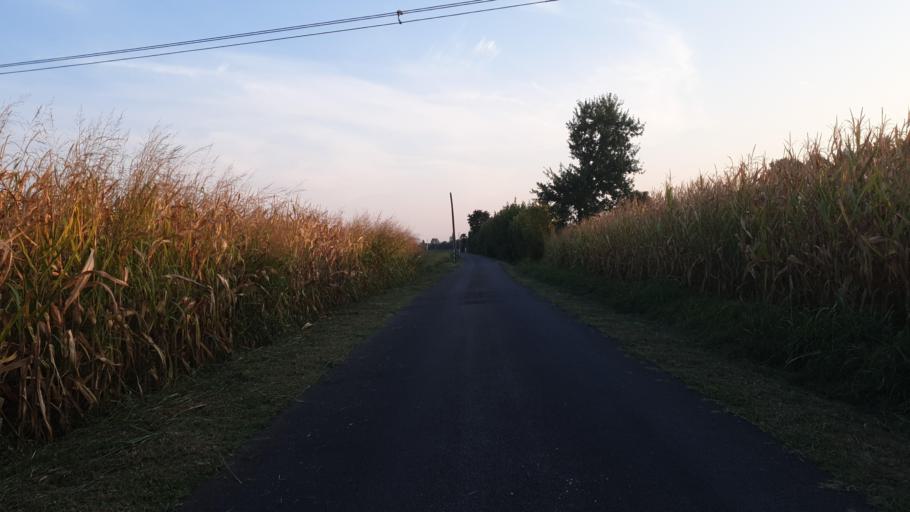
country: IT
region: Veneto
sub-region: Provincia di Padova
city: Albignasego
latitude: 45.3613
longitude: 11.8787
